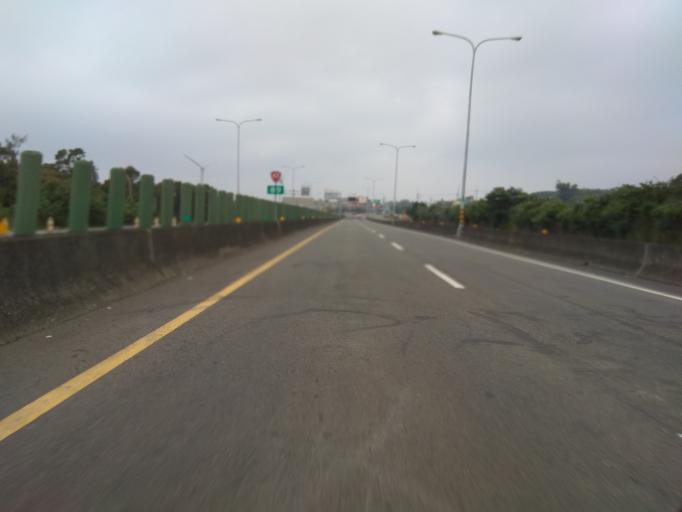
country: TW
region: Taiwan
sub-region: Hsinchu
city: Hsinchu
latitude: 24.7097
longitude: 120.8673
